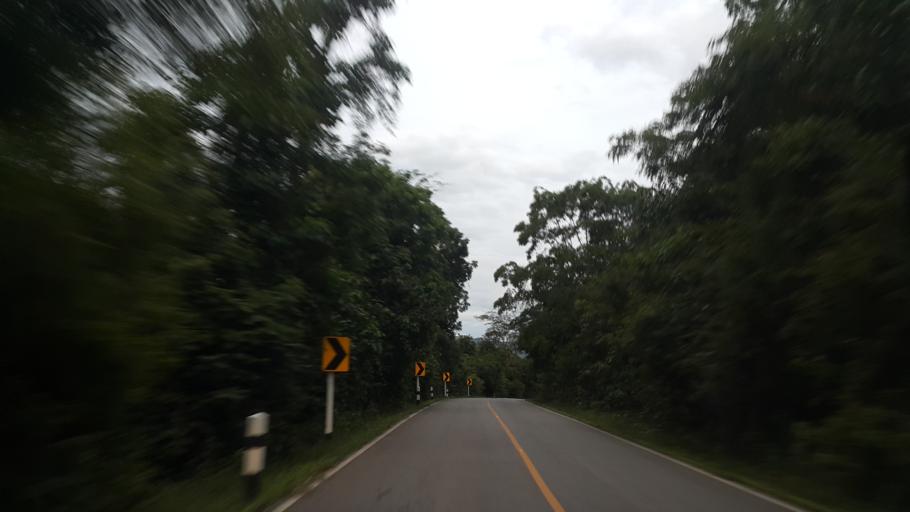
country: TH
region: Loei
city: Na Haeo
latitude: 17.5303
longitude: 101.1987
